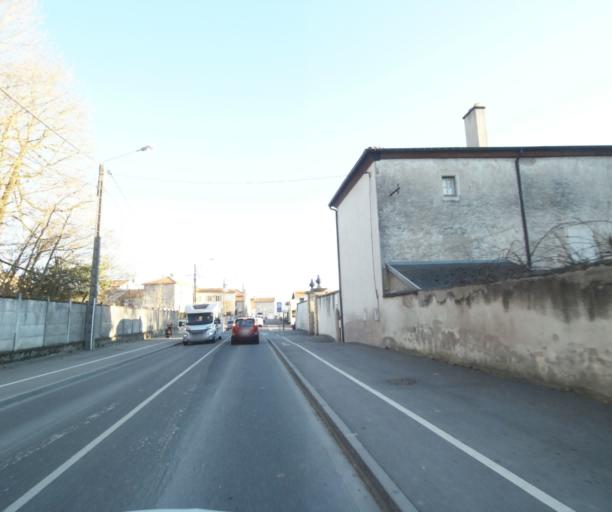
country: FR
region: Lorraine
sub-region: Departement de Meurthe-et-Moselle
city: Art-sur-Meurthe
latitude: 48.6568
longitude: 6.2637
